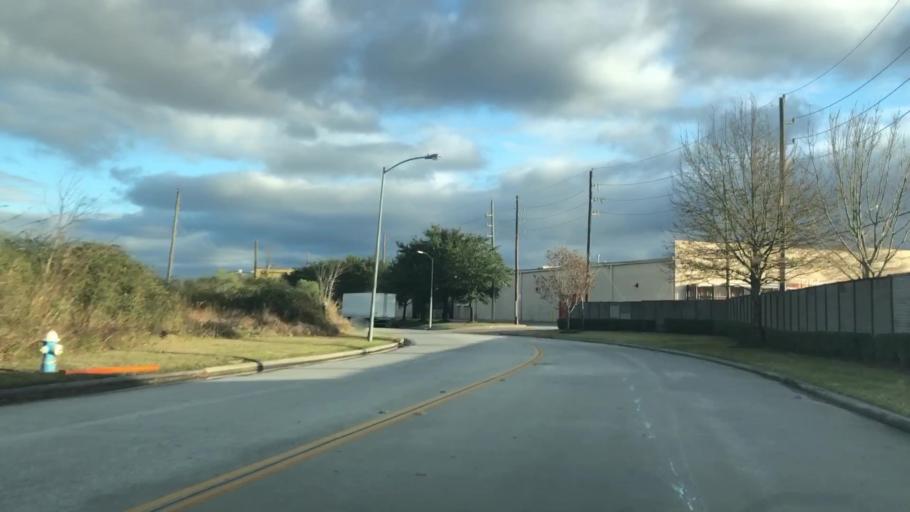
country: US
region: Texas
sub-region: Harris County
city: Aldine
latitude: 29.9190
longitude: -95.4164
